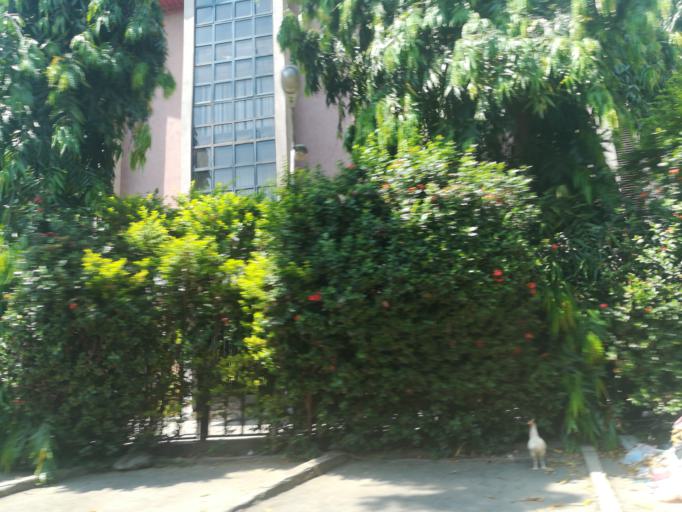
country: NG
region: Abuja Federal Capital Territory
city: Abuja
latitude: 9.0734
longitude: 7.4483
